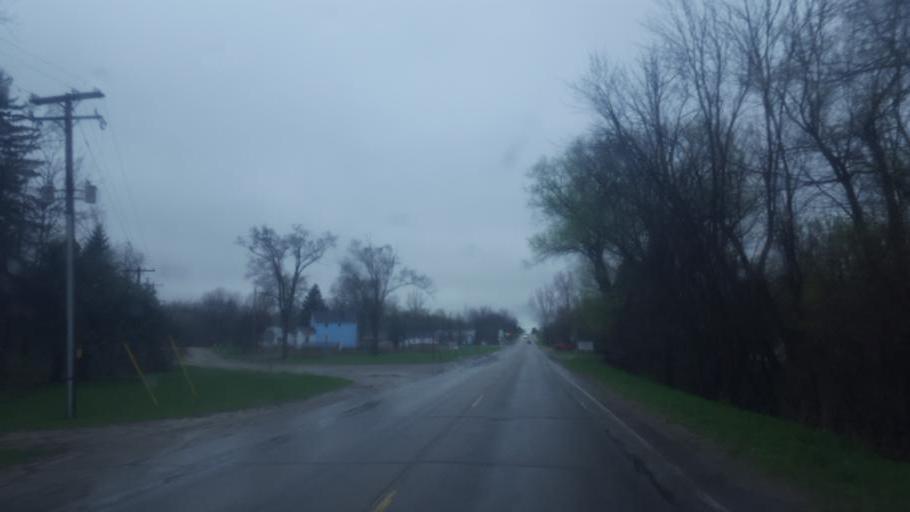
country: US
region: Michigan
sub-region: Isabella County
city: Mount Pleasant
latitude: 43.6259
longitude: -84.7680
